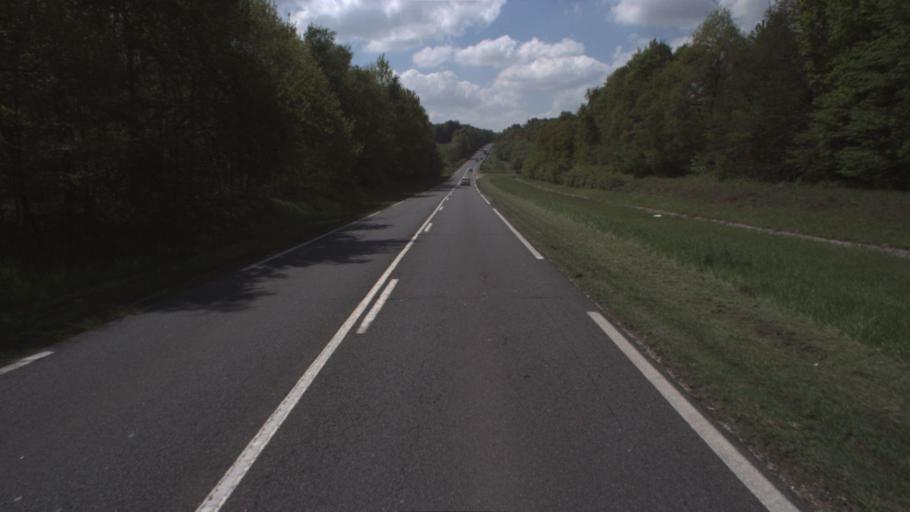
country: FR
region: Ile-de-France
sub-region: Departement de Seine-et-Marne
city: Guignes
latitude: 48.6611
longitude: 2.8093
